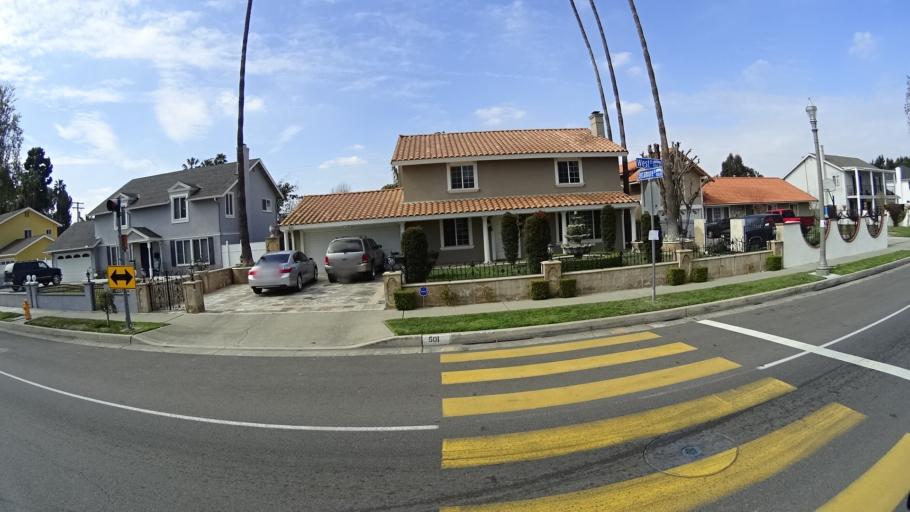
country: US
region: California
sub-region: Orange County
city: Anaheim
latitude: 33.8369
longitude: -117.9285
